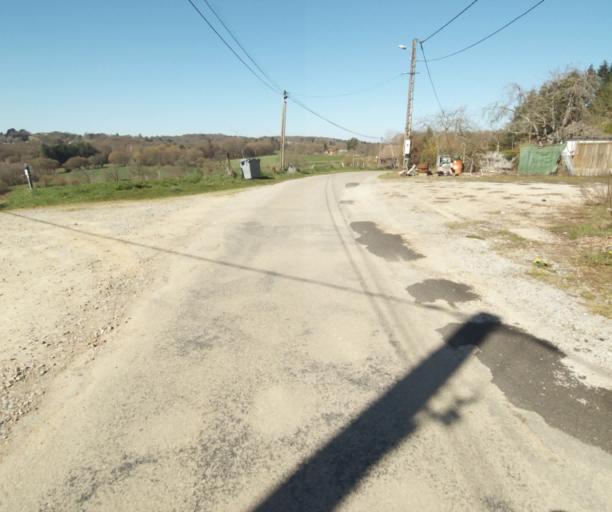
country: FR
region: Limousin
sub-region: Departement de la Correze
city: Saint-Clement
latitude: 45.3063
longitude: 1.7164
